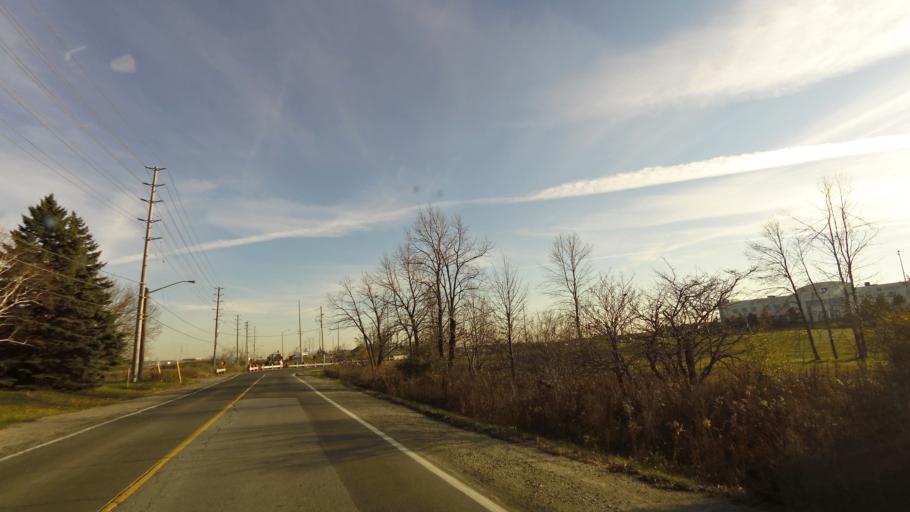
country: CA
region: Ontario
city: Brampton
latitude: 43.7561
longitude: -79.6885
